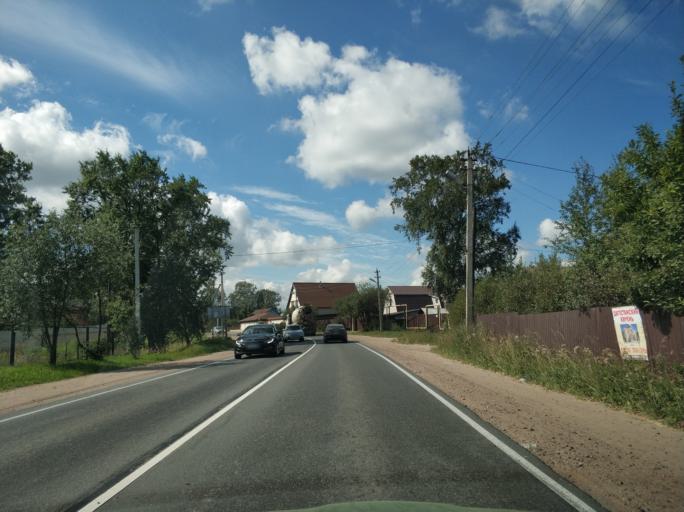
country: RU
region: Leningrad
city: Romanovka
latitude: 60.0523
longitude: 30.7274
